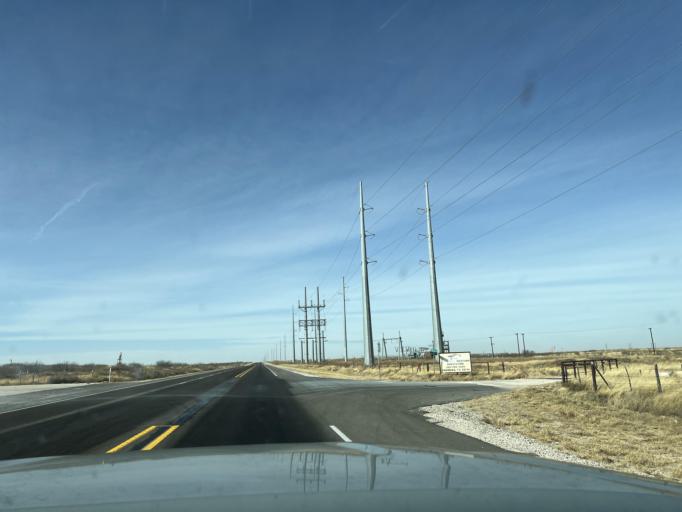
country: US
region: Texas
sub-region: Andrews County
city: Andrews
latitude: 32.3503
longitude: -102.7342
